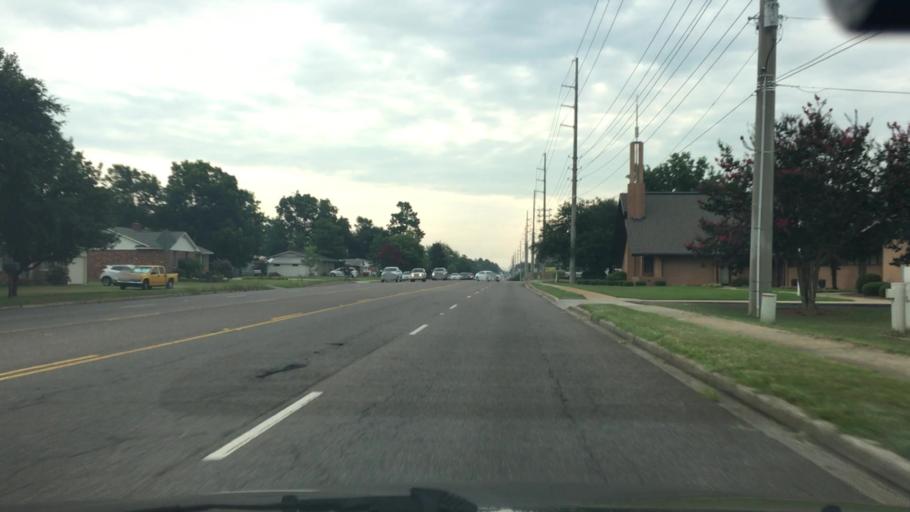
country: US
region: South Carolina
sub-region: Aiken County
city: Aiken
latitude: 33.5264
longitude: -81.7121
